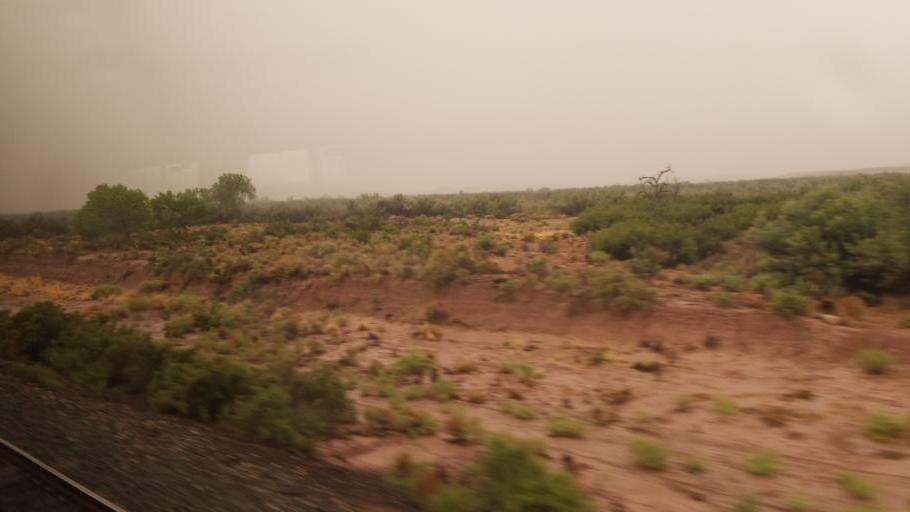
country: US
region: Arizona
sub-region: Navajo County
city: Joseph City
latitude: 34.9535
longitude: -110.3529
